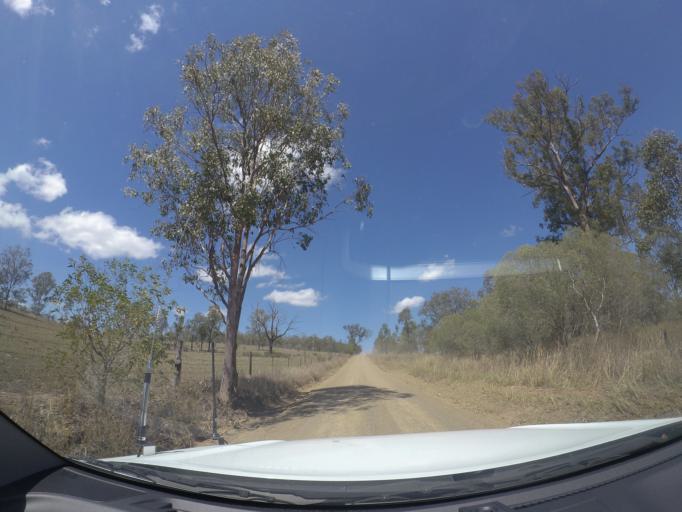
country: AU
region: Queensland
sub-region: Logan
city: Cedar Vale
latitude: -27.8538
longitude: 152.8859
